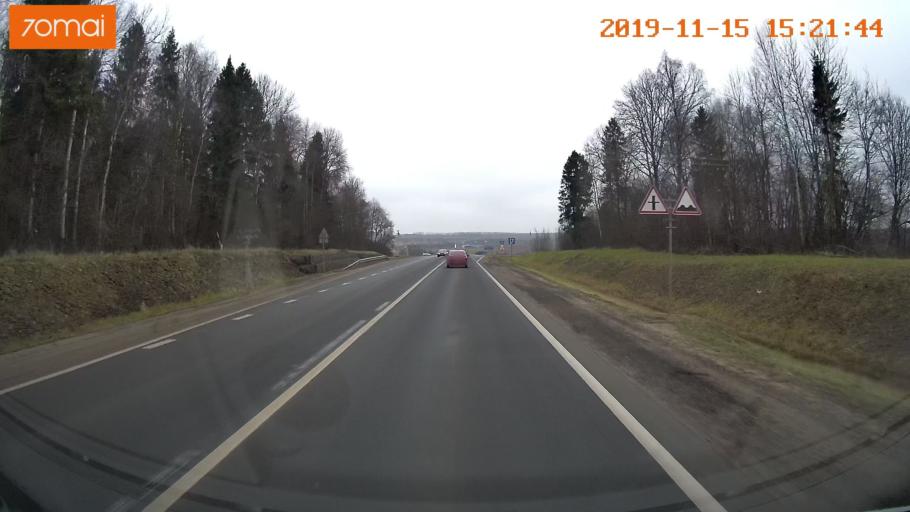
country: RU
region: Jaroslavl
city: Danilov
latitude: 58.2096
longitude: 40.1412
